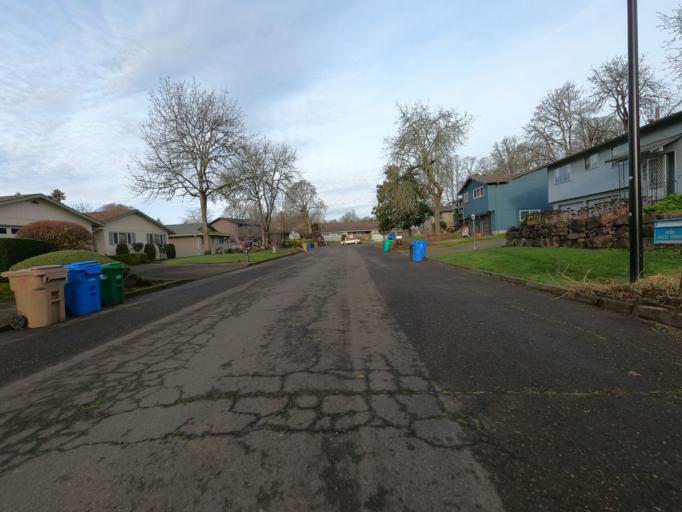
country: US
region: Oregon
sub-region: Clackamas County
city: Jennings Lodge
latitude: 45.3966
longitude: -122.6081
